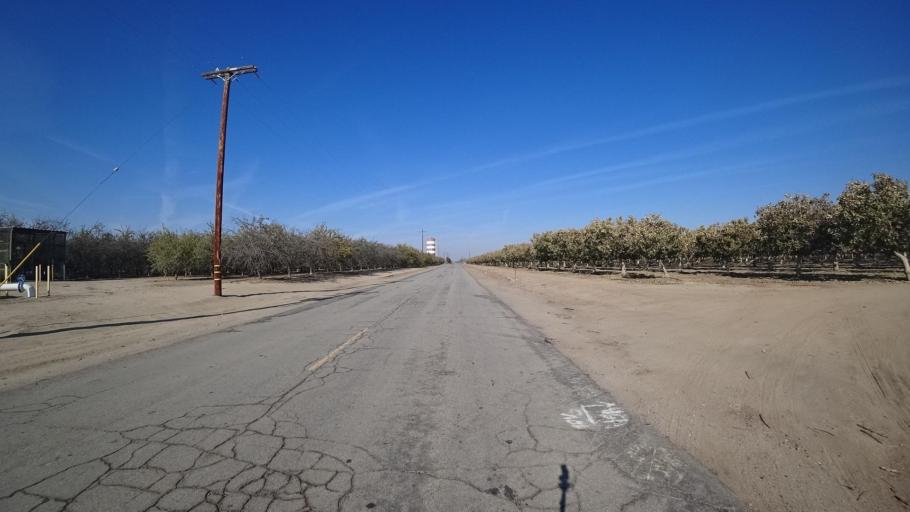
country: US
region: California
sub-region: Kern County
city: Wasco
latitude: 35.6558
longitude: -119.3486
